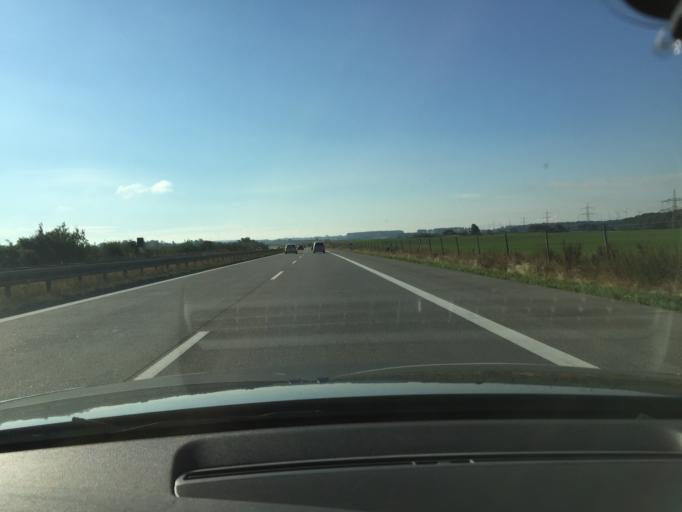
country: DE
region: Mecklenburg-Vorpommern
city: Kavelstorf
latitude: 53.9640
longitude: 12.1971
